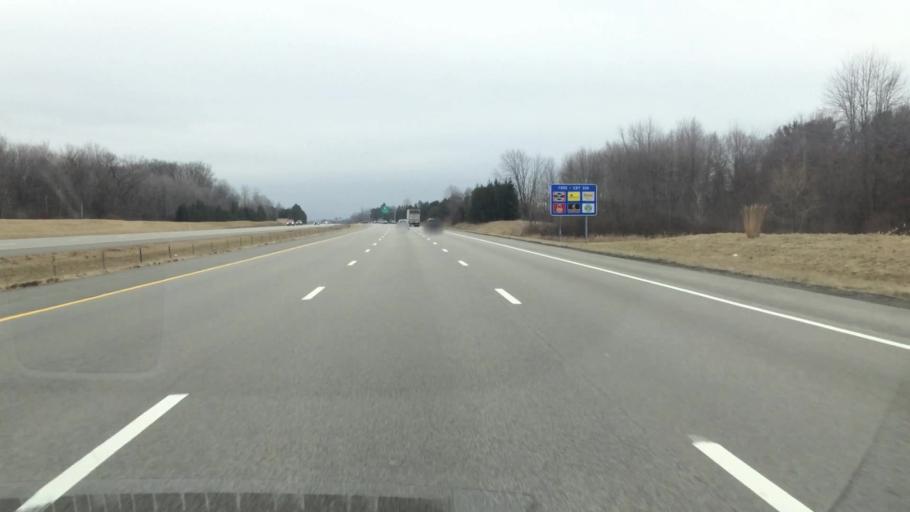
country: US
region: Ohio
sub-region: Medina County
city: Brunswick
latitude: 41.2598
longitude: -81.8046
